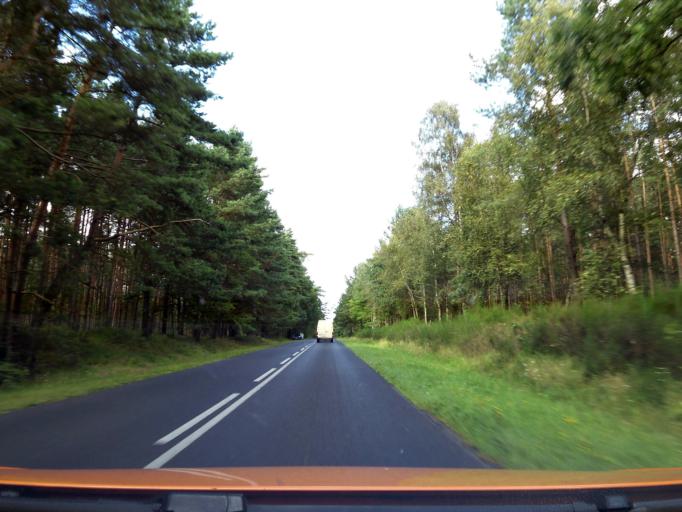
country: PL
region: West Pomeranian Voivodeship
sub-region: Powiat kolobrzeski
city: Kolobrzeg
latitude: 54.1101
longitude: 15.5848
